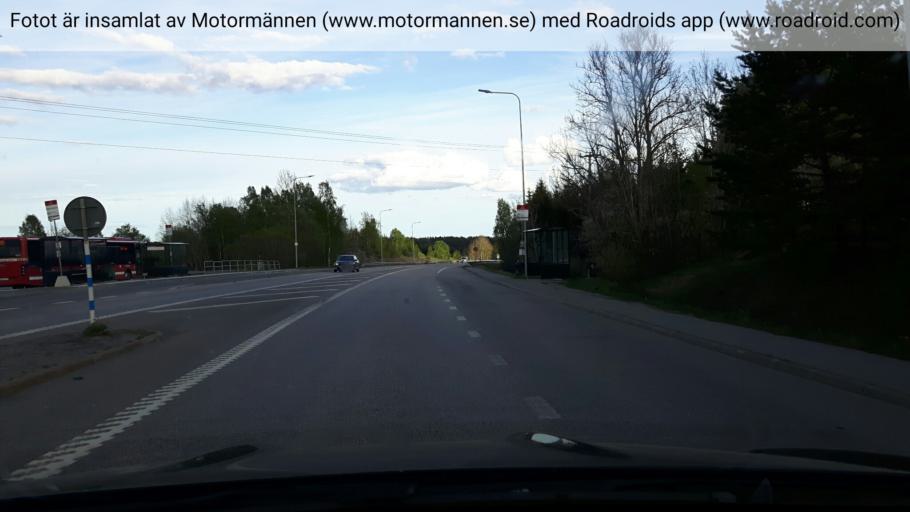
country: SE
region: Stockholm
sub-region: Osterakers Kommun
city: Akersberga
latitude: 59.4500
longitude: 18.2161
